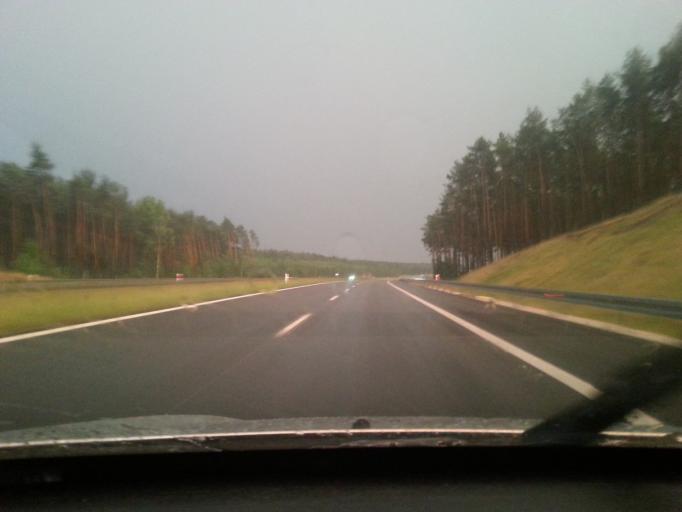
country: PL
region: Lodz Voivodeship
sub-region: Powiat pabianicki
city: Dobron
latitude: 51.6251
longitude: 19.2728
